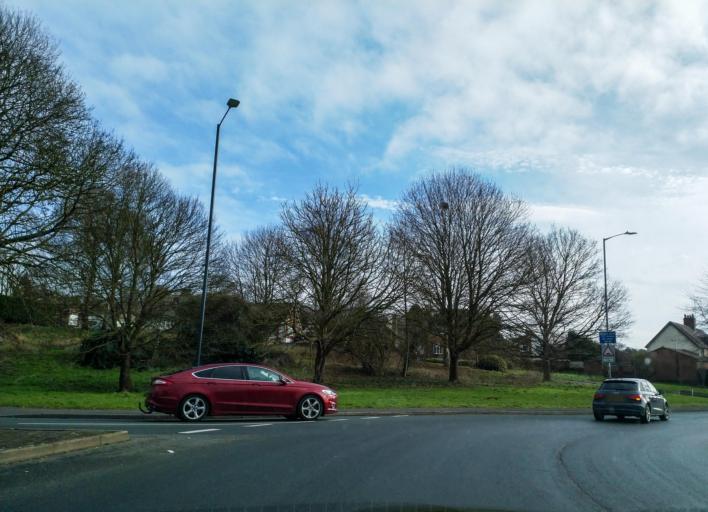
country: GB
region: England
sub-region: Warwickshire
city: Warwick
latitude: 52.2942
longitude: -1.5766
